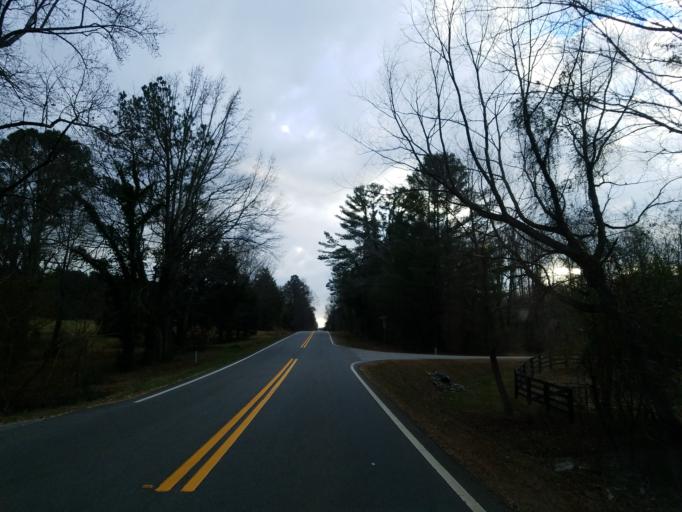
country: US
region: Georgia
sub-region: Dawson County
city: Dawsonville
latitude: 34.3341
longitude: -84.0667
